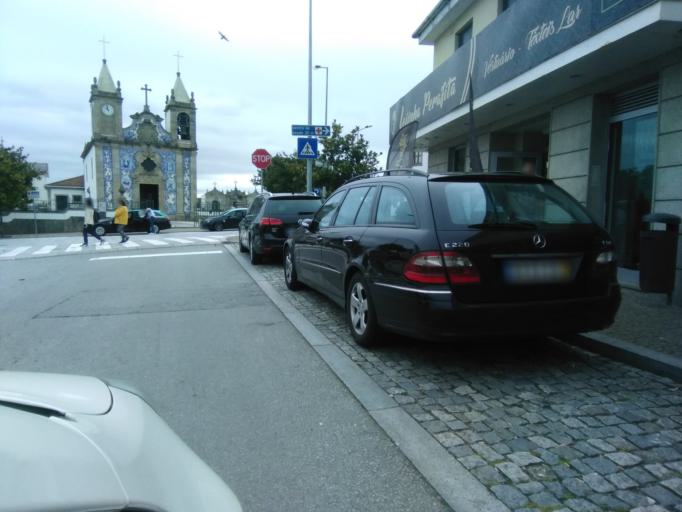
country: PT
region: Porto
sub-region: Matosinhos
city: Santa Cruz do Bispo
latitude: 41.2244
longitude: -8.6981
